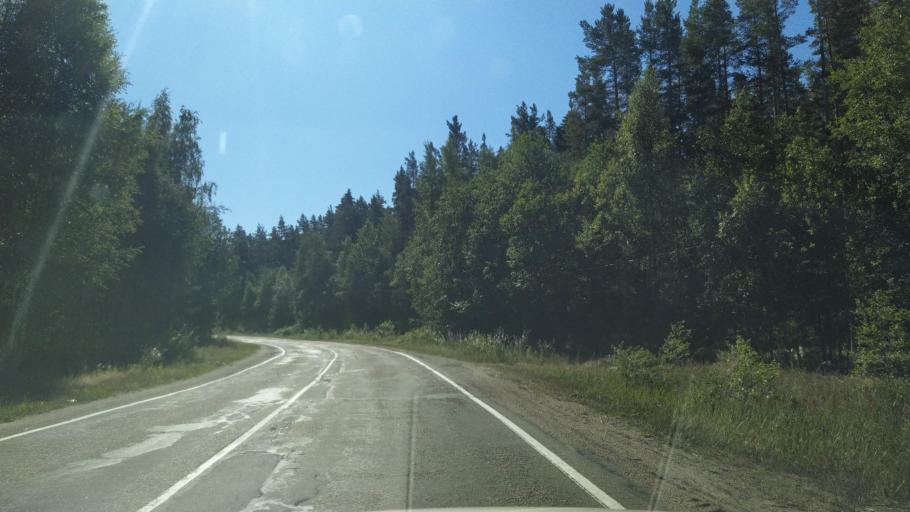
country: RU
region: Leningrad
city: Priozersk
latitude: 60.9899
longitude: 30.2583
